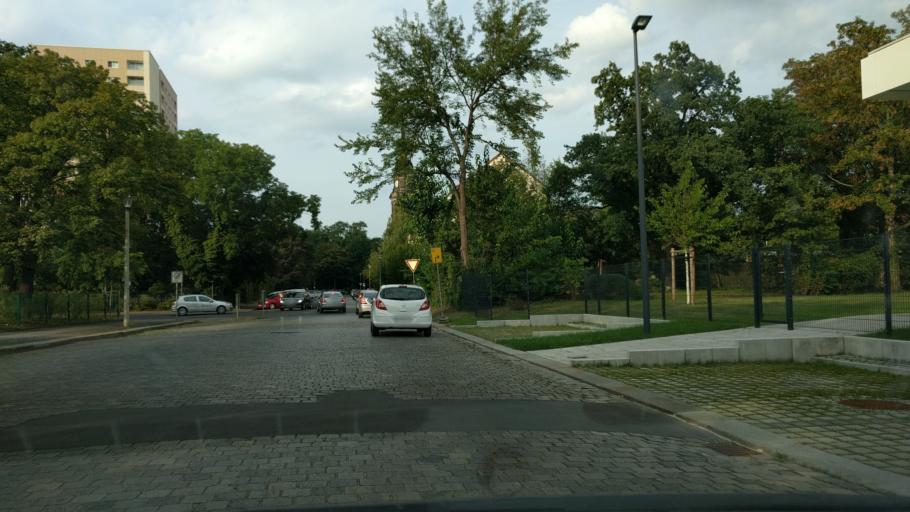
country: DE
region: Saxony
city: Dresden
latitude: 51.0506
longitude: 13.7695
